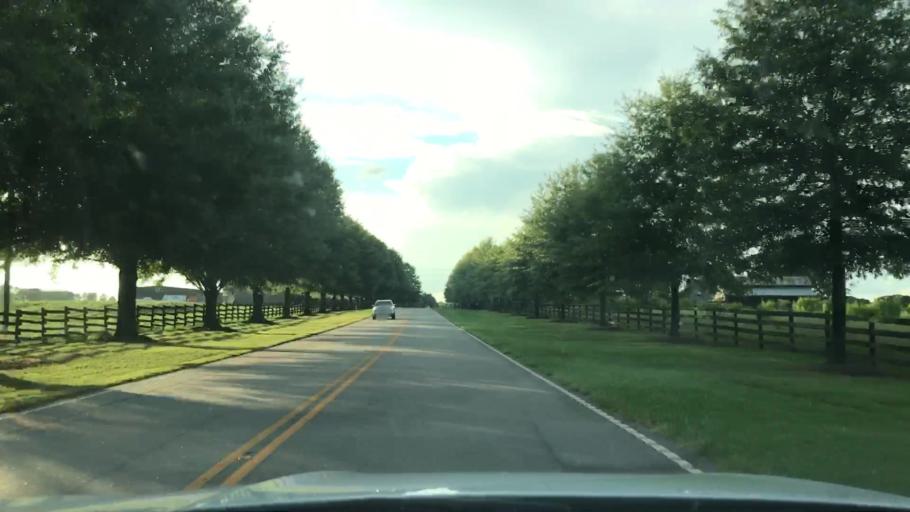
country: US
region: South Carolina
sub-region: Spartanburg County
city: Roebuck
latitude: 34.8111
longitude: -81.9220
